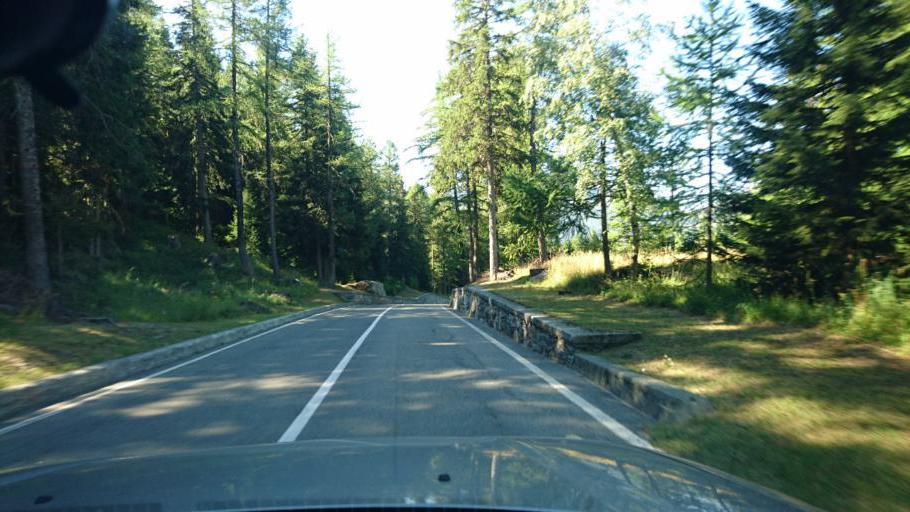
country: IT
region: Aosta Valley
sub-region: Valle d'Aosta
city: Pre Saint Didier
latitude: 45.7351
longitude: 6.9752
